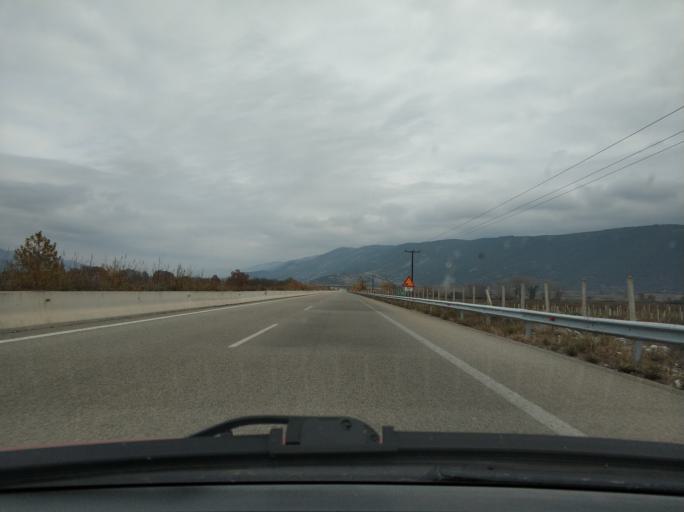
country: GR
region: Central Macedonia
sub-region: Nomos Serron
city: Rodolivos
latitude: 40.8227
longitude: 24.0708
